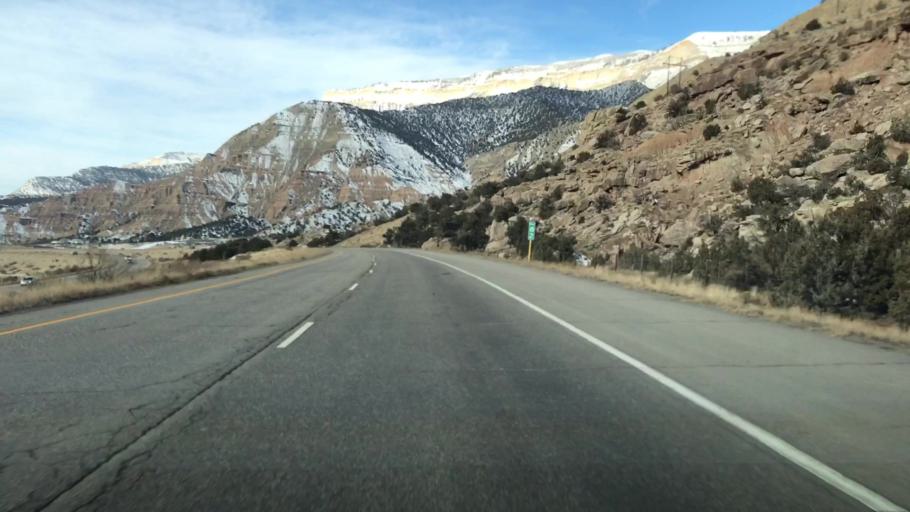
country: US
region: Colorado
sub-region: Garfield County
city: Battlement Mesa
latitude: 39.5009
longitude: -107.9284
